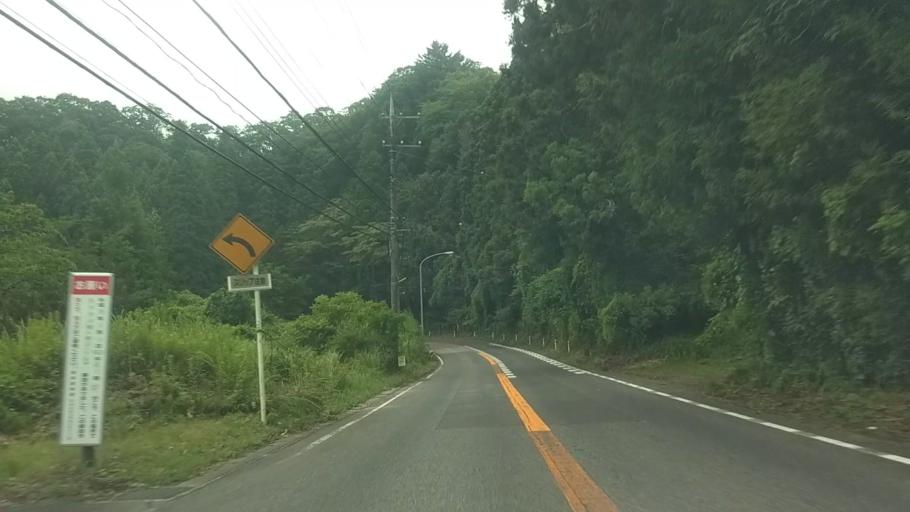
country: JP
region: Chiba
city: Kawaguchi
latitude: 35.2091
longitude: 140.0679
